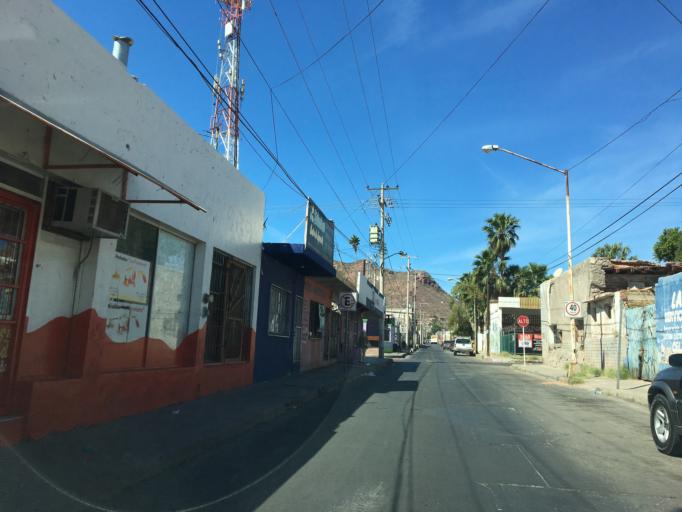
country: MX
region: Sonora
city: Heroica Guaymas
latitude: 27.9225
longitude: -110.8963
